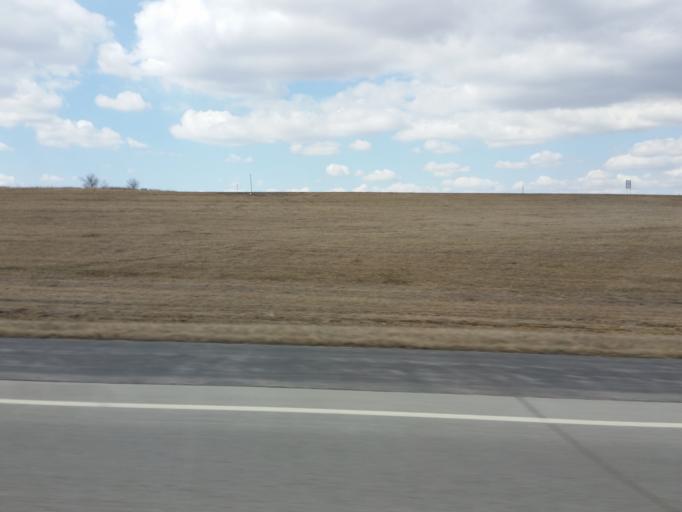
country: US
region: South Dakota
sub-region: Roberts County
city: Sisseton
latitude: 45.4015
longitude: -97.0225
